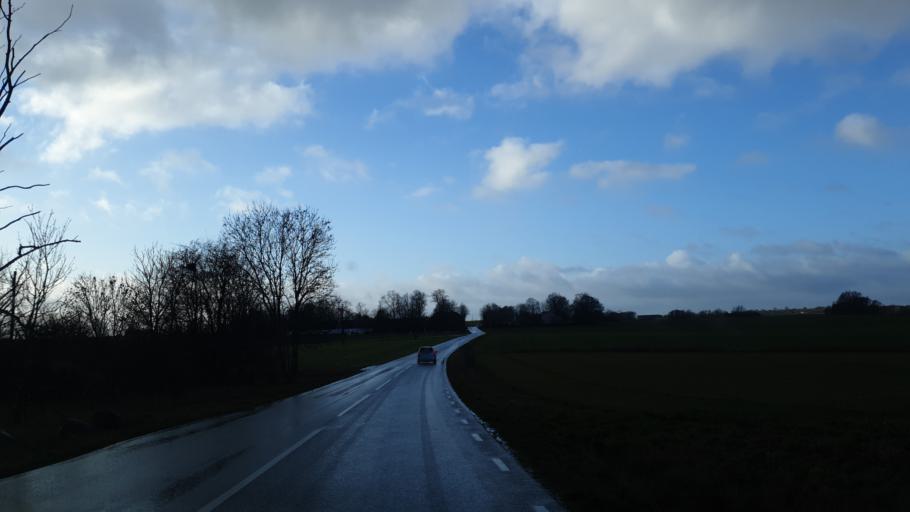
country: SE
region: Skane
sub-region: Skurups Kommun
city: Rydsgard
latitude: 55.4683
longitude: 13.5732
